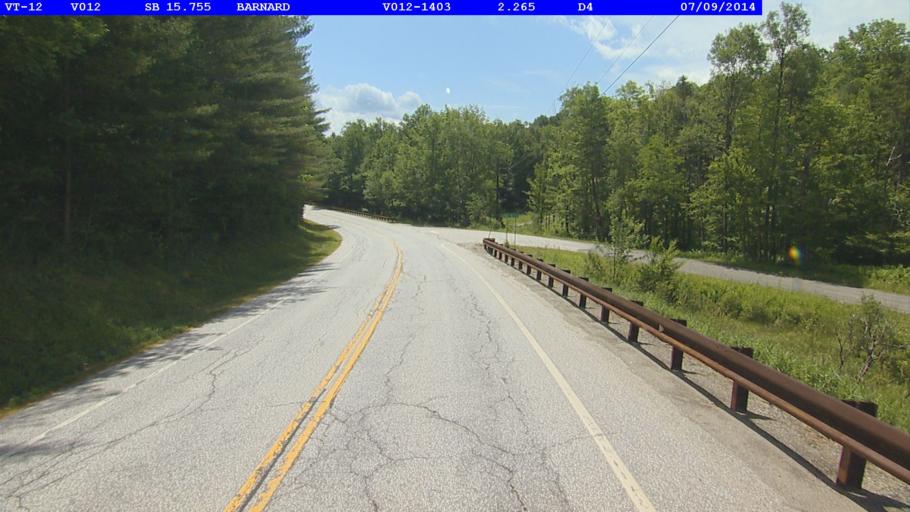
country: US
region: Vermont
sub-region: Windsor County
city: Woodstock
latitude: 43.6959
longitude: -72.6146
